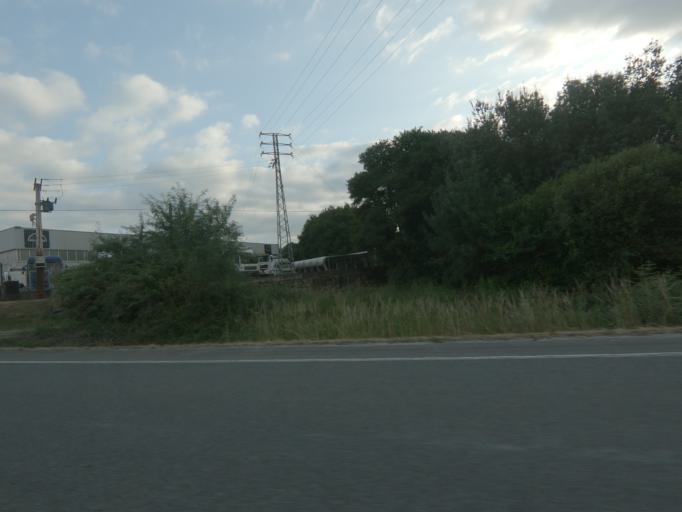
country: ES
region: Galicia
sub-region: Provincia de Ourense
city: Taboadela
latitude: 42.2793
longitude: -7.8370
